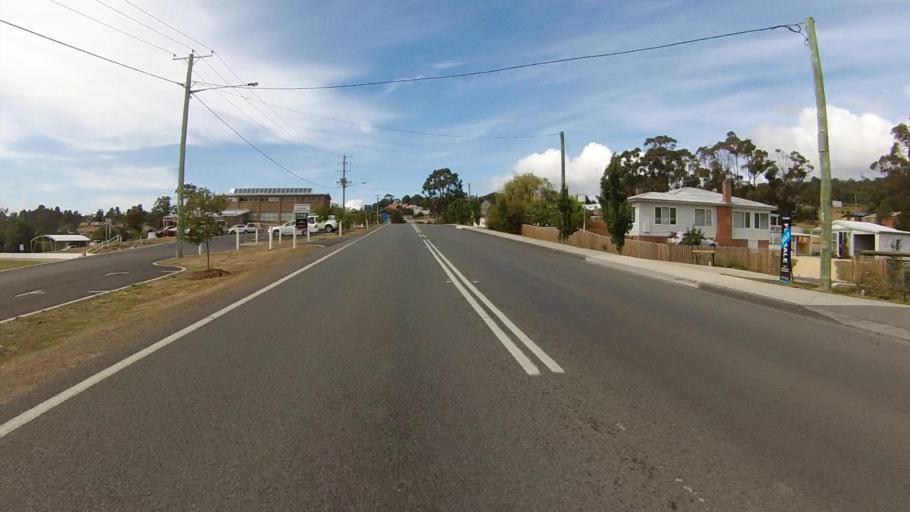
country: AU
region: Tasmania
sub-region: Kingborough
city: Kettering
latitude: -43.1244
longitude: 147.2454
